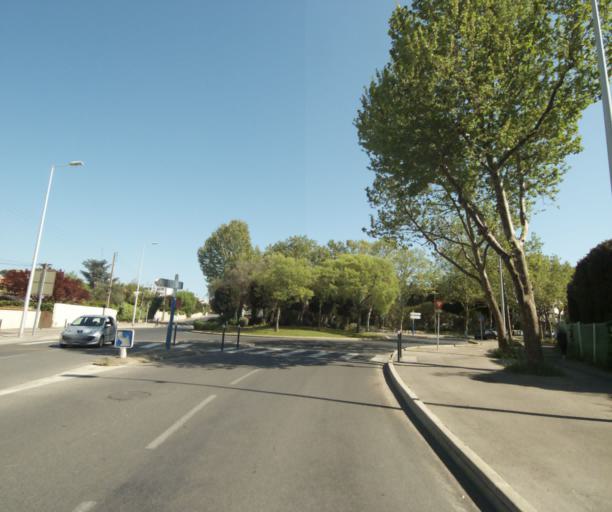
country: FR
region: Languedoc-Roussillon
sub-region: Departement de l'Herault
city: Montpellier
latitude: 43.6203
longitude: 3.8585
